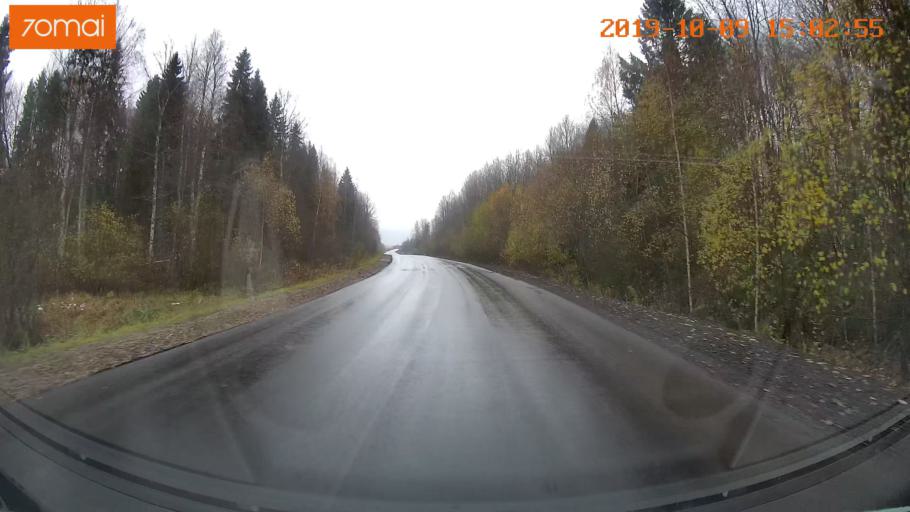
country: RU
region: Kostroma
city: Chistyye Bory
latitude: 58.2785
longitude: 41.6767
